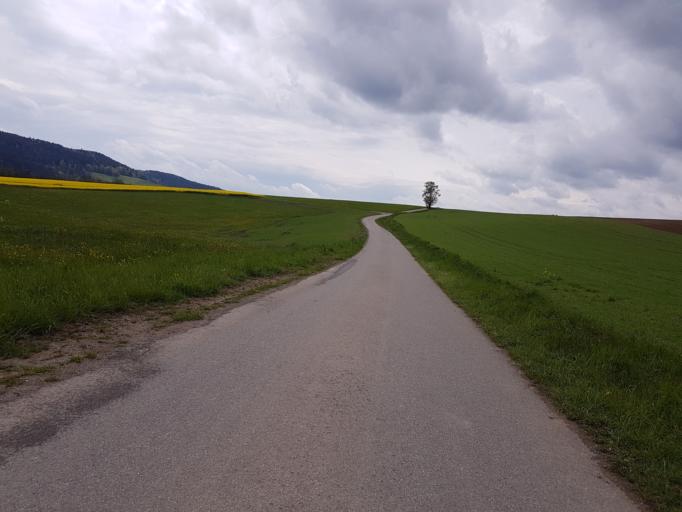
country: DE
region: Baden-Wuerttemberg
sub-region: Freiburg Region
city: Blumberg
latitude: 47.8024
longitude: 8.5194
